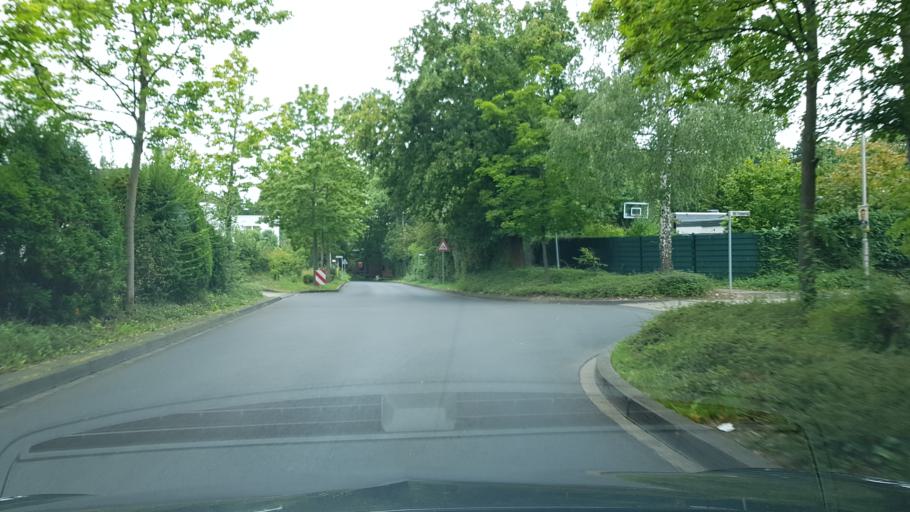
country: DE
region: North Rhine-Westphalia
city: Meckenheim
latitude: 50.6261
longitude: 7.0284
